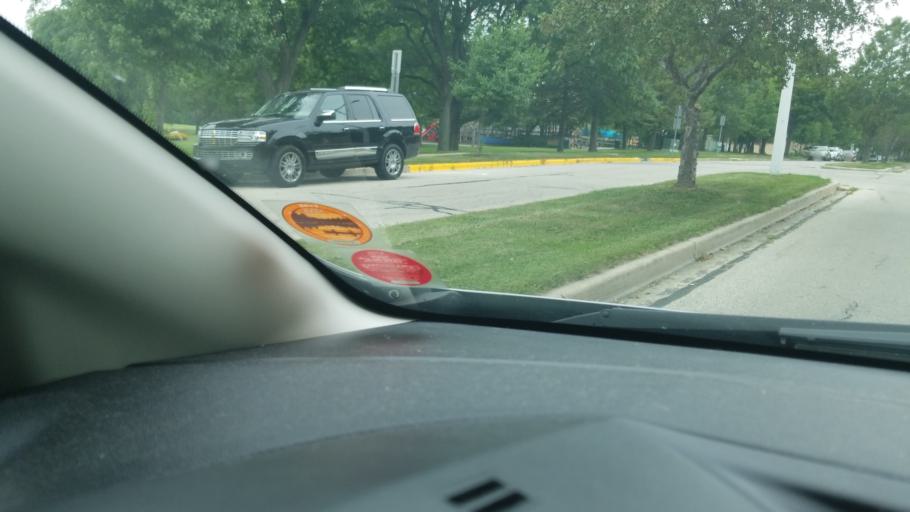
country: US
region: Wisconsin
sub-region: Ozaukee County
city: Cedarburg
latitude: 43.3050
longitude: -87.9946
